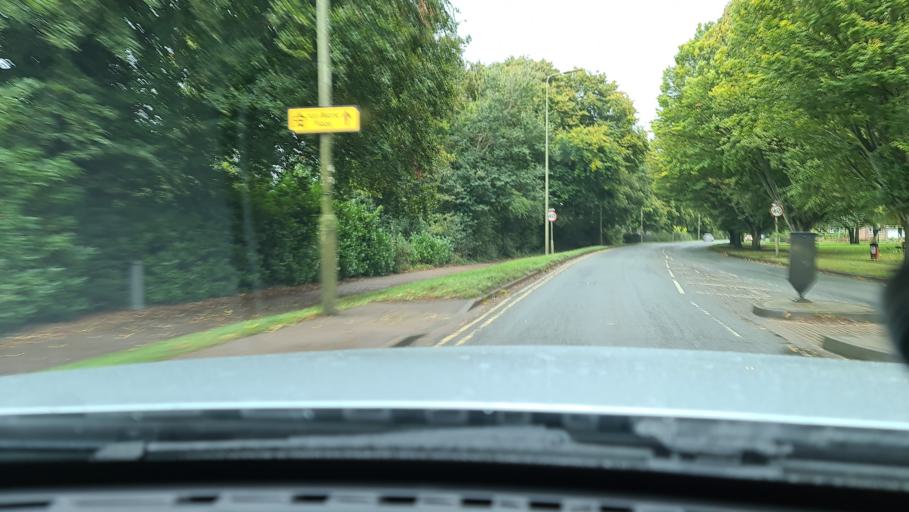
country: GB
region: England
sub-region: Oxfordshire
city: Banbury
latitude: 52.0493
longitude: -1.3340
